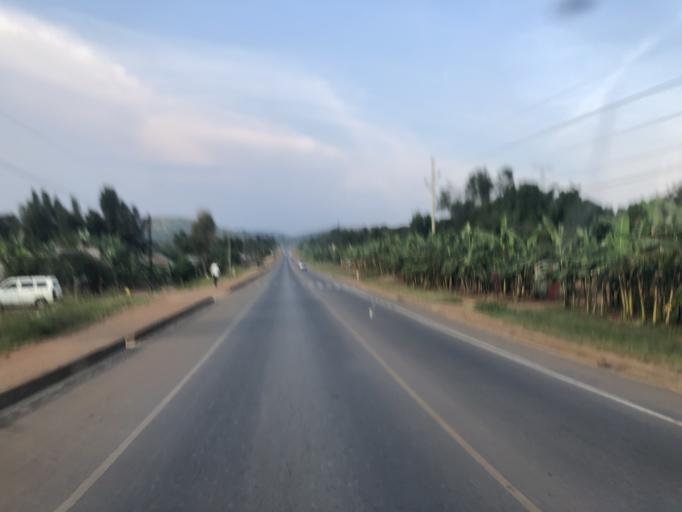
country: UG
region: Central Region
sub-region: Mpigi District
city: Mpigi
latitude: 0.1748
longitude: 32.2748
